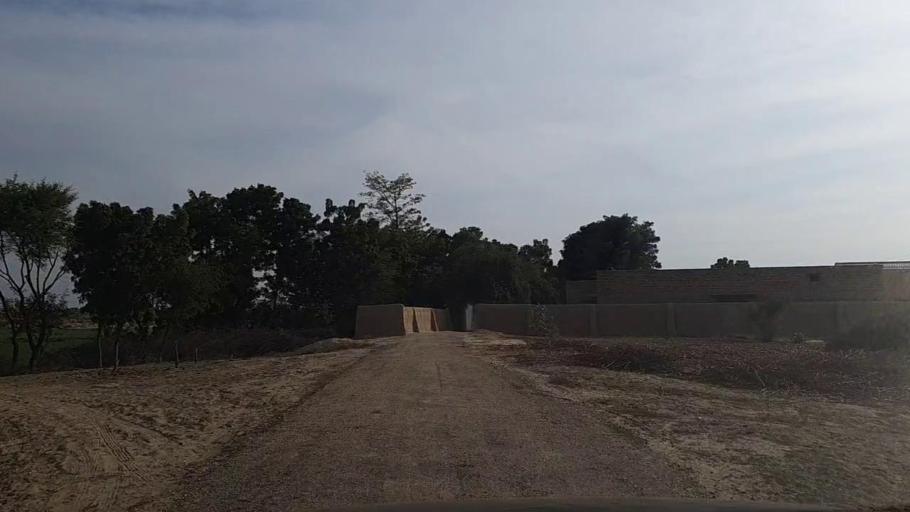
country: PK
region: Sindh
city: Jam Sahib
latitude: 26.4465
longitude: 68.6104
